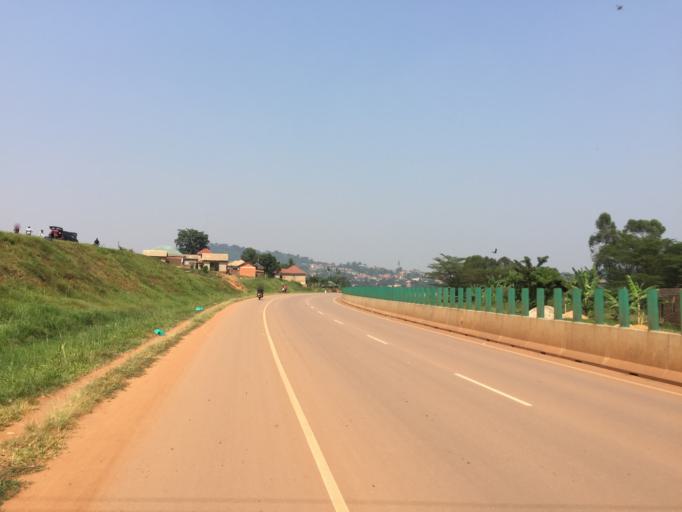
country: UG
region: Central Region
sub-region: Kampala District
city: Kampala
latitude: 0.2338
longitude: 32.6080
